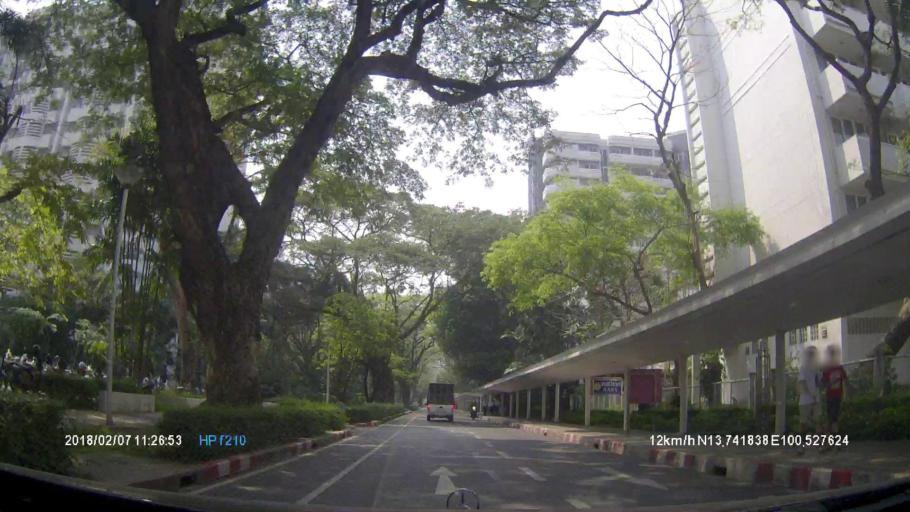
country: TH
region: Bangkok
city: Pathum Wan
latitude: 13.7416
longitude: 100.5276
